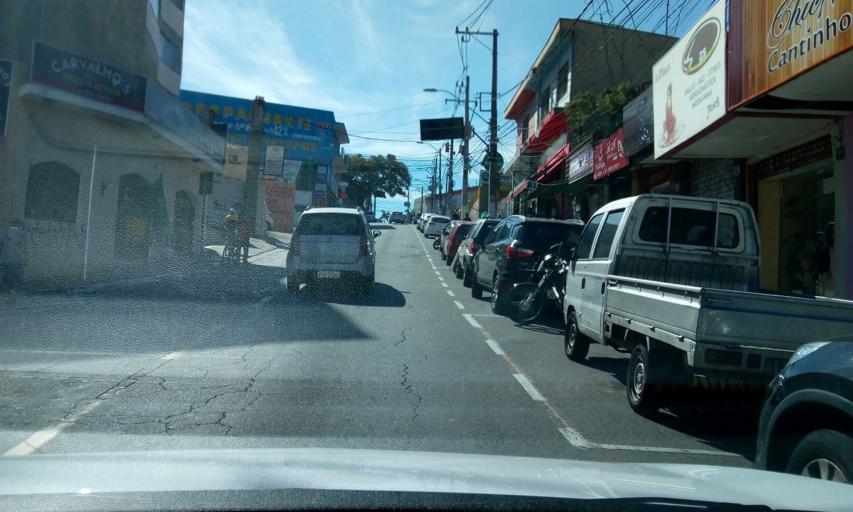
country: BR
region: Sao Paulo
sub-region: Barueri
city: Barueri
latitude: -23.5082
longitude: -46.8757
